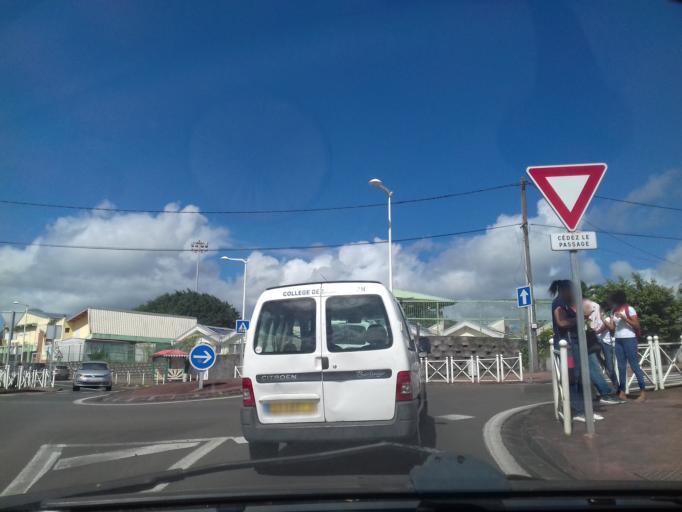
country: MQ
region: Martinique
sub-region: Martinique
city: Saint-Joseph
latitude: 14.6724
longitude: -61.0335
